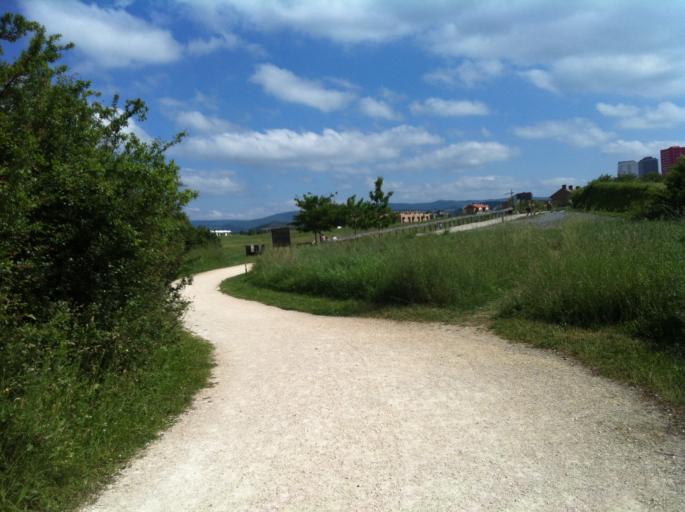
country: ES
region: Basque Country
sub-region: Provincia de Alava
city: Gasteiz / Vitoria
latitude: 42.8548
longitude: -2.6479
